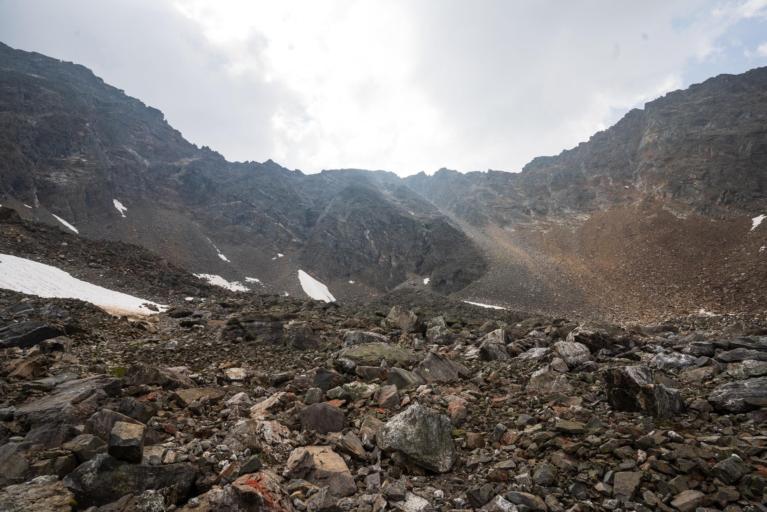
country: RU
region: Transbaikal Territory
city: Chara
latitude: 56.8129
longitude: 117.1234
